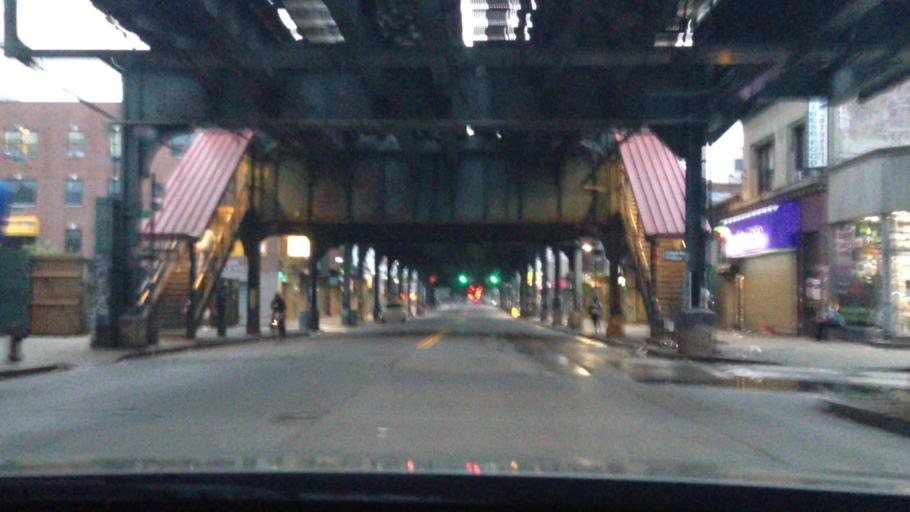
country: US
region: New York
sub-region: Kings County
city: East New York
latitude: 40.6903
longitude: -73.9235
